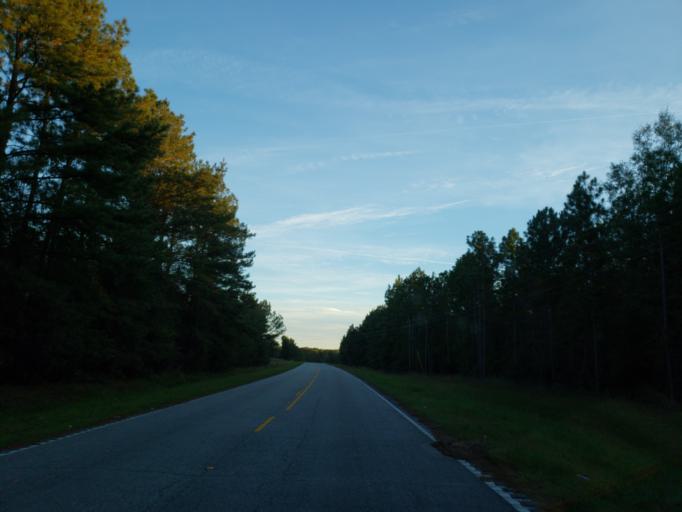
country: US
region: Mississippi
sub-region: Wayne County
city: Belmont
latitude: 31.4117
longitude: -88.4712
